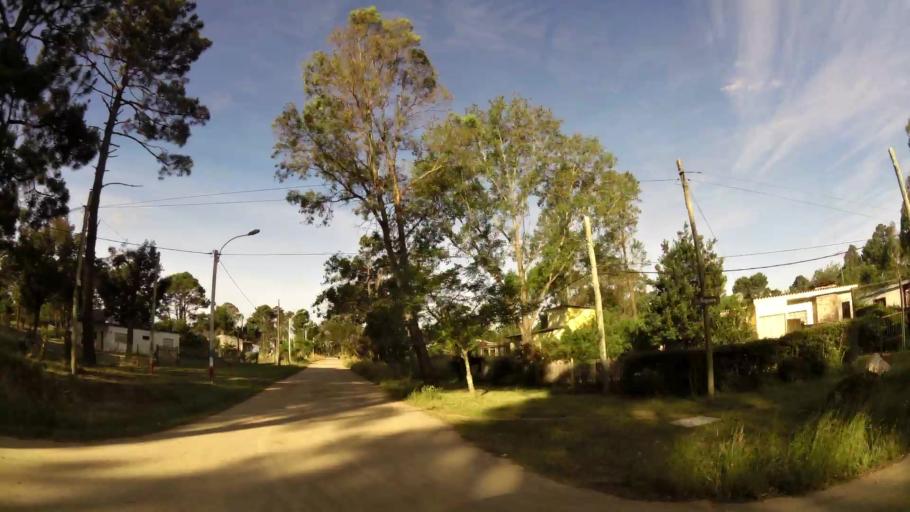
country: UY
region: Canelones
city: Empalme Olmos
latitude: -34.7727
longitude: -55.8569
